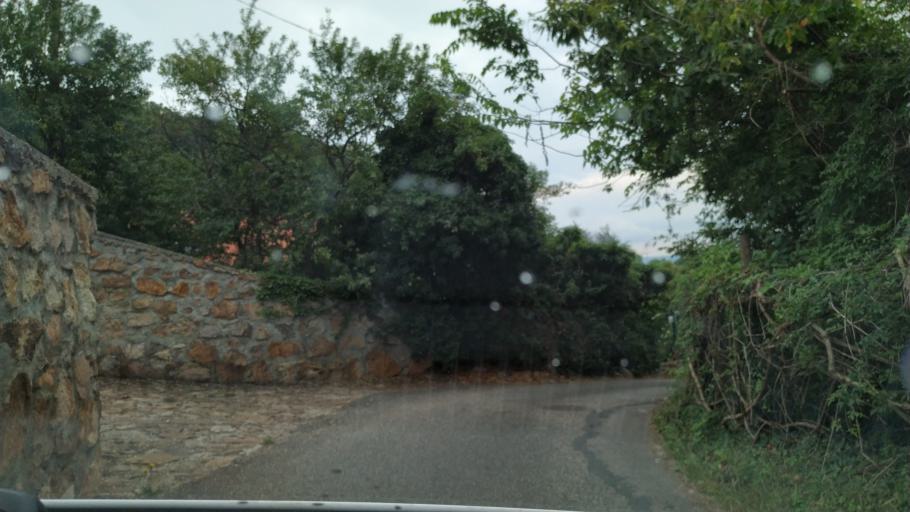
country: HU
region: Veszprem
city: Badacsonytomaj
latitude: 46.8097
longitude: 17.5471
